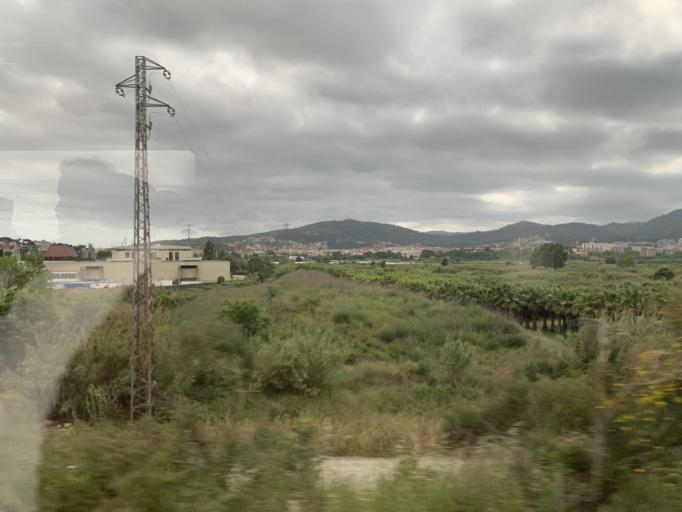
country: ES
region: Catalonia
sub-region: Provincia de Barcelona
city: Sant Boi de Llobregat
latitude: 41.3555
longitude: 2.0506
